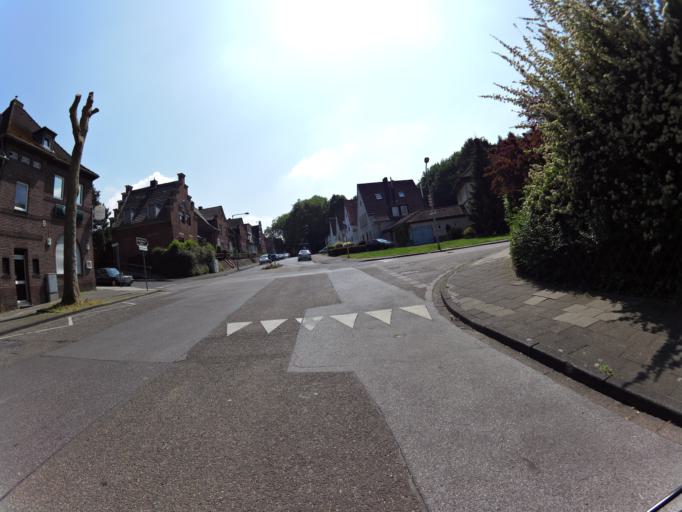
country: DE
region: North Rhine-Westphalia
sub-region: Regierungsbezirk Koln
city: Herzogenrath
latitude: 50.8959
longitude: 6.1224
